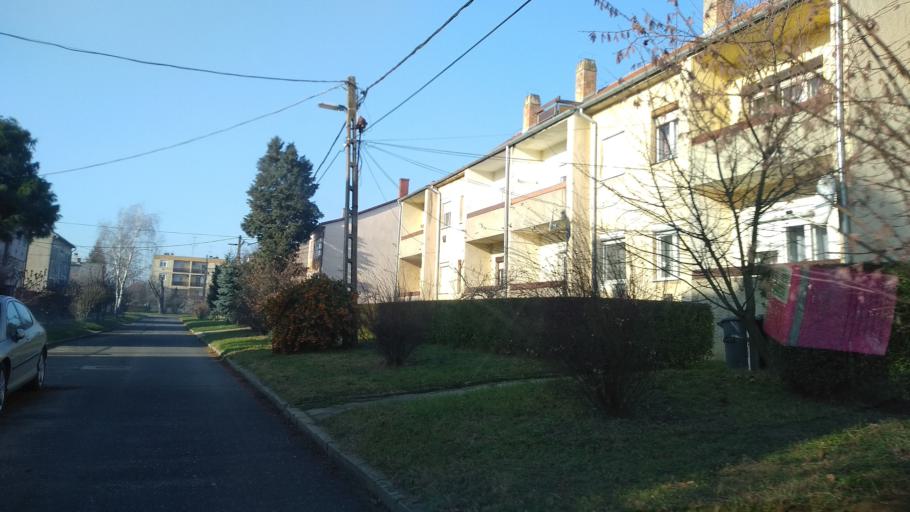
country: HU
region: Somogy
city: Barcs
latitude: 45.9607
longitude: 17.4573
